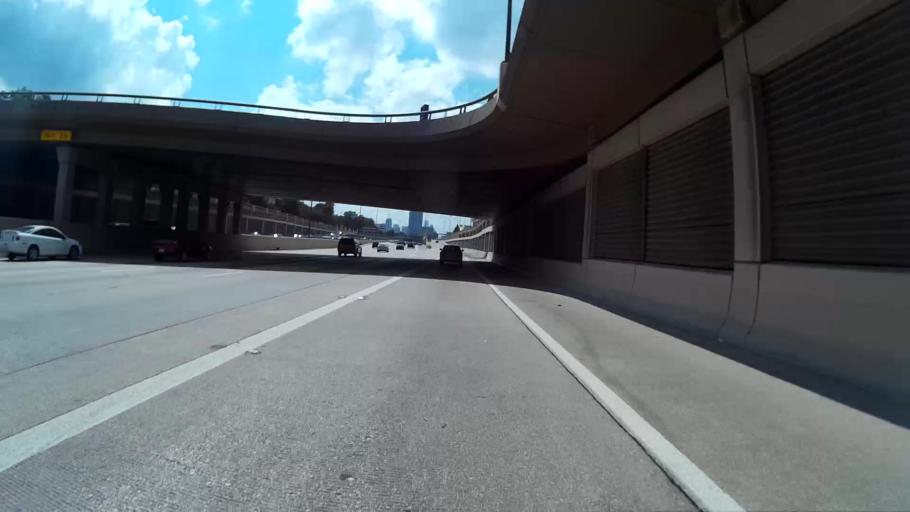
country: US
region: Texas
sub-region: Dallas County
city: Highland Park
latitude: 32.8270
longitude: -96.7839
